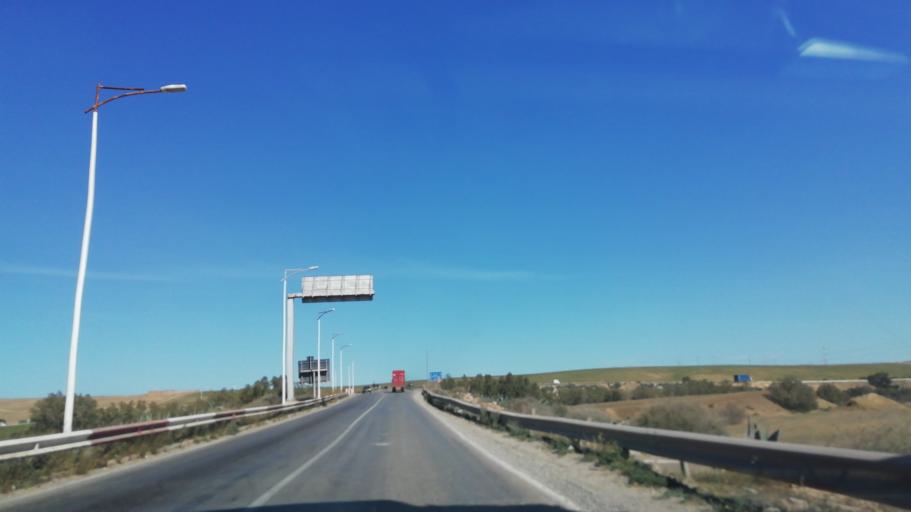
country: DZ
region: Oran
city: Sidi ech Chahmi
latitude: 35.5711
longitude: -0.5577
